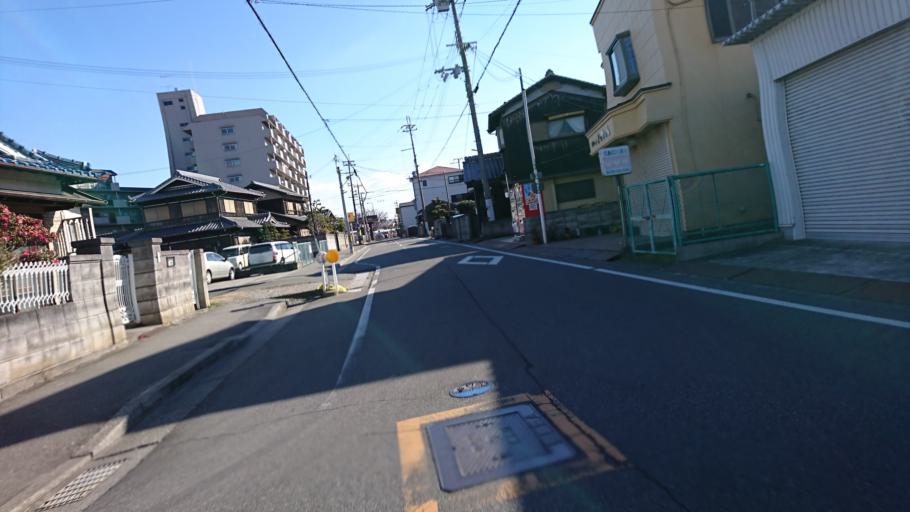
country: JP
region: Hyogo
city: Kakogawacho-honmachi
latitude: 34.7222
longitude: 134.8859
